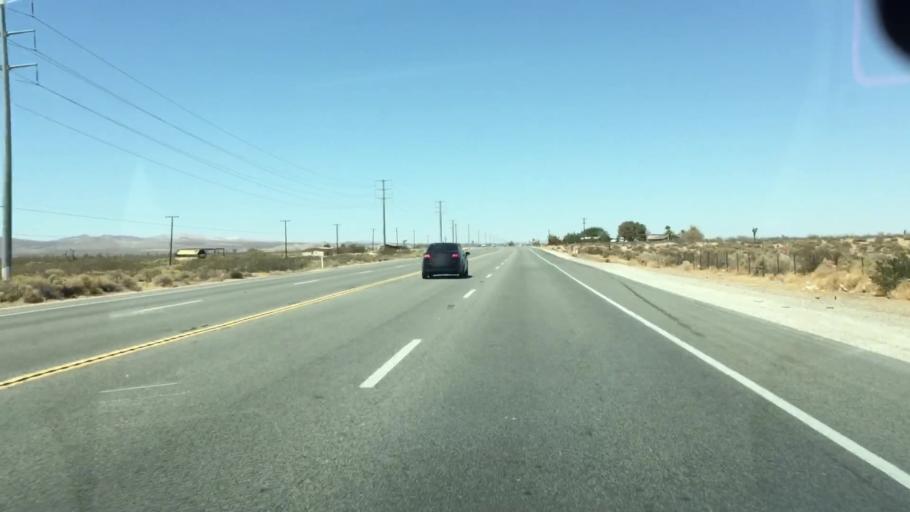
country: US
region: California
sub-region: San Bernardino County
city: Adelanto
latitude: 34.5973
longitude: -117.4182
